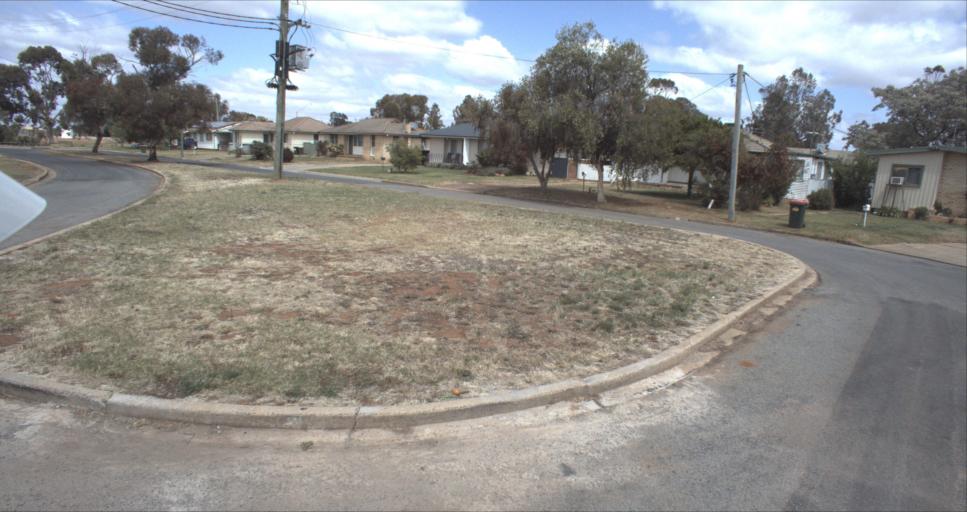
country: AU
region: New South Wales
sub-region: Leeton
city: Leeton
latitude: -34.5670
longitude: 146.3948
